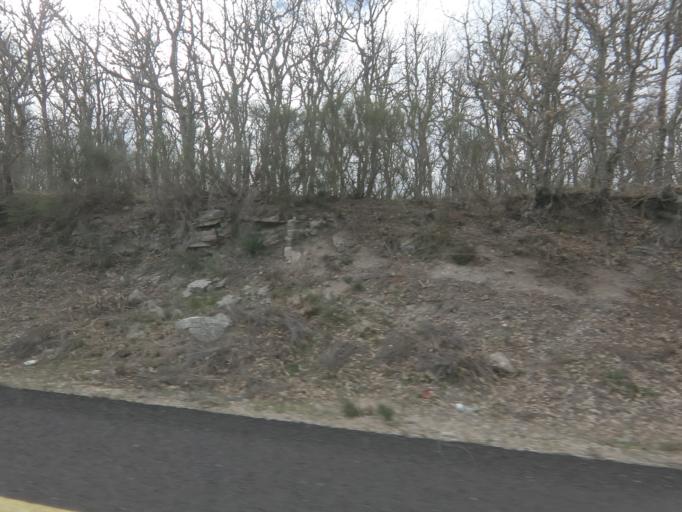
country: ES
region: Castille and Leon
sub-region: Provincia de Salamanca
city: Penaparda
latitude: 40.2858
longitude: -6.6706
